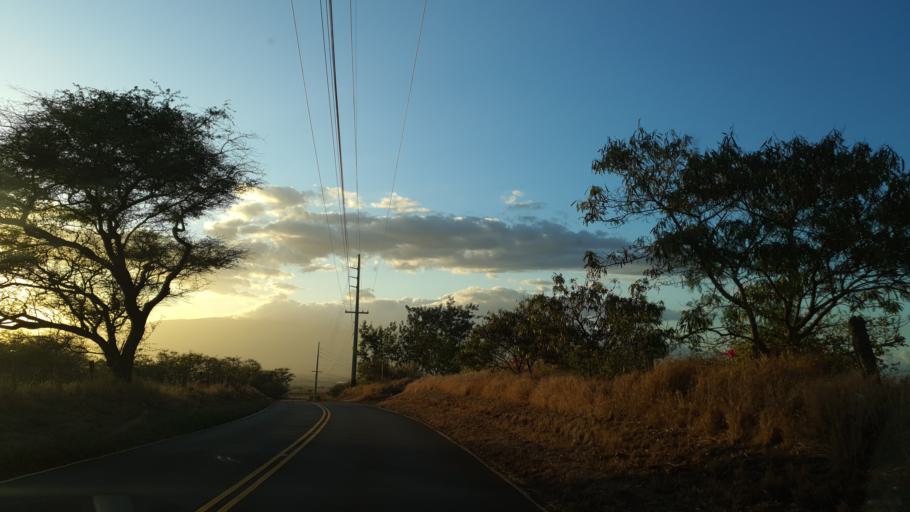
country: US
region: Hawaii
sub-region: Maui County
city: Pukalani
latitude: 20.7954
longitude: -156.3674
